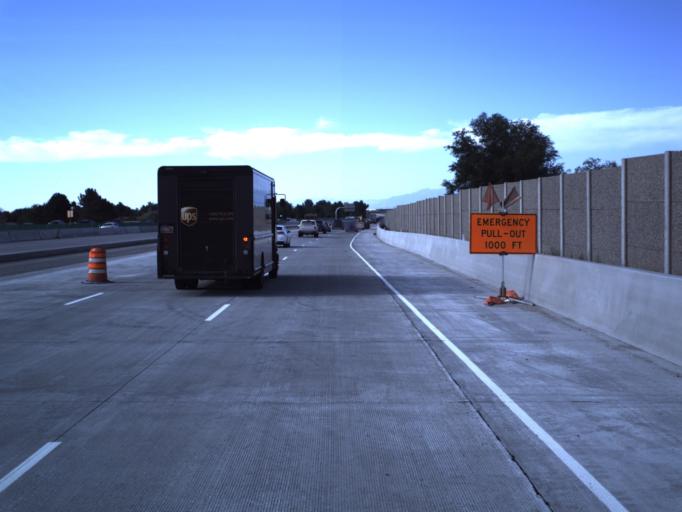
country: US
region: Utah
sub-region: Salt Lake County
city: Taylorsville
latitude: 40.6736
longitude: -111.9523
